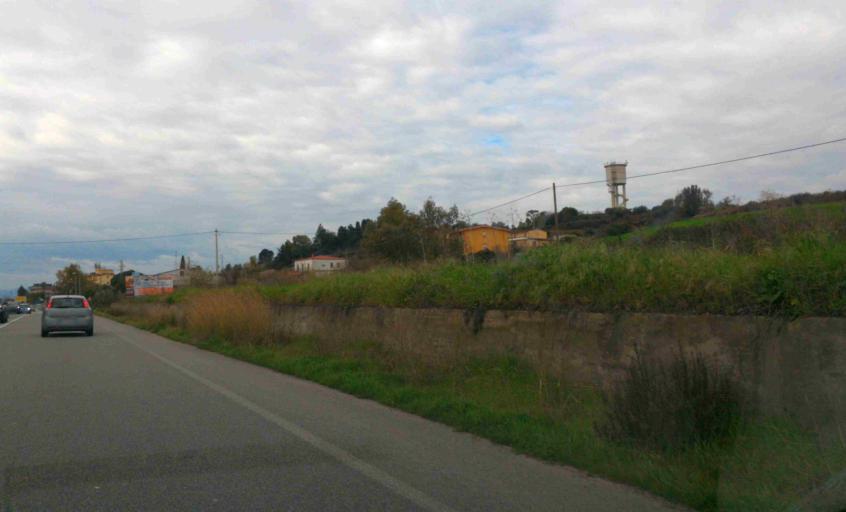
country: IT
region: Calabria
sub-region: Provincia di Catanzaro
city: Sellia Marina
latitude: 38.8896
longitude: 16.7181
